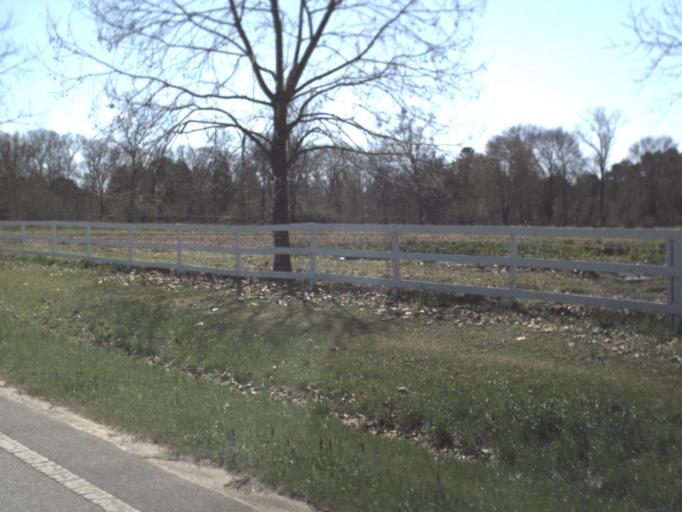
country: US
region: Florida
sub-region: Gadsden County
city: Gretna
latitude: 30.6557
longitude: -84.6042
